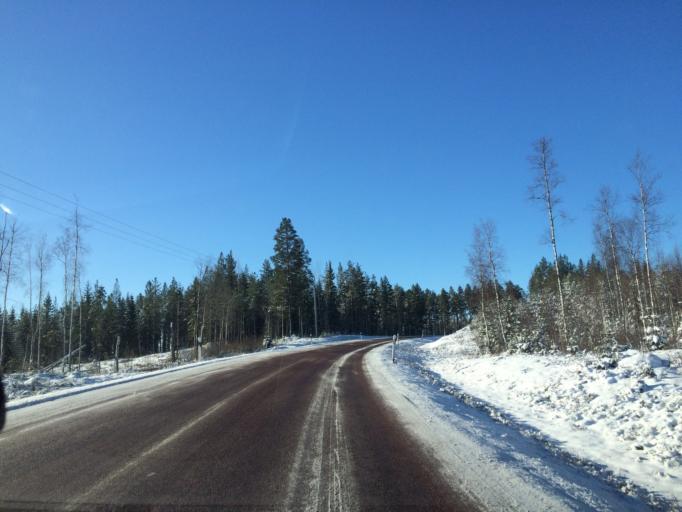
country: SE
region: Dalarna
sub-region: Vansbro Kommun
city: Vansbro
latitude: 60.8479
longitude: 14.2066
